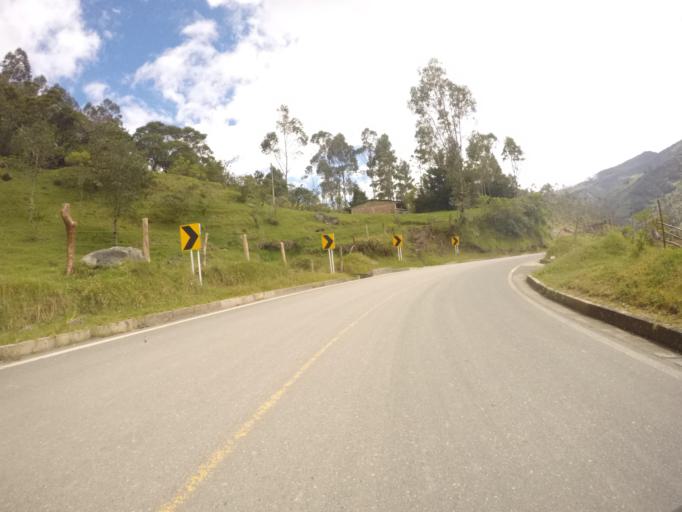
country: CO
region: Cauca
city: Jambalo
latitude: 2.7259
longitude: -76.3245
